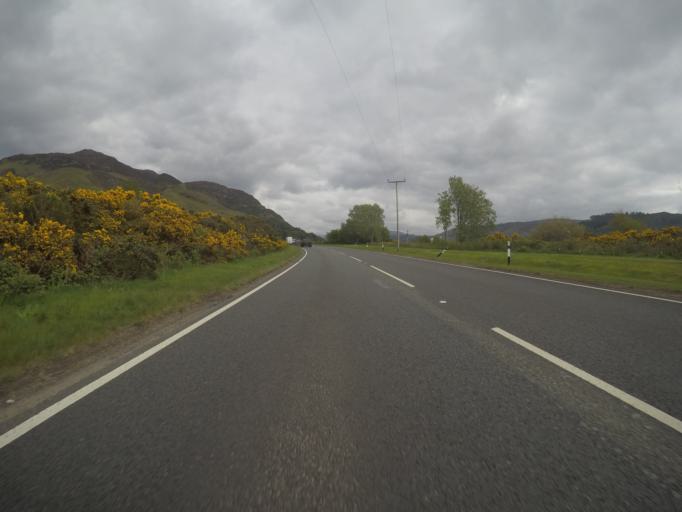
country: GB
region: Scotland
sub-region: Highland
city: Fort William
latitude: 57.2796
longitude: -5.5216
